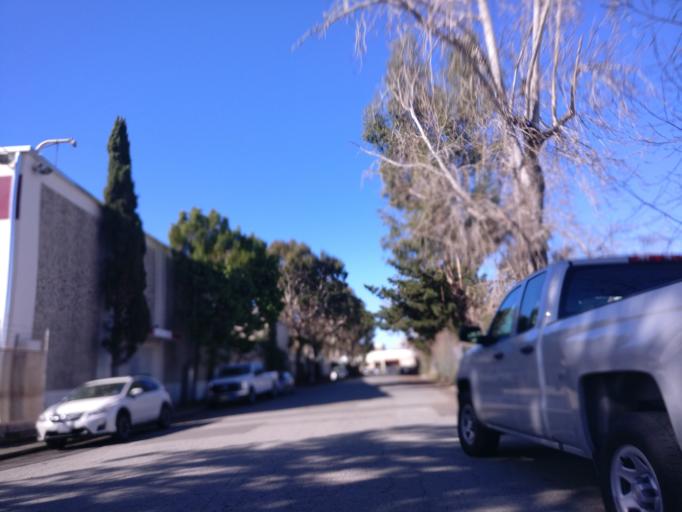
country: US
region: California
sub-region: Alameda County
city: Oakland
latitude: 37.7923
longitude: -122.2648
